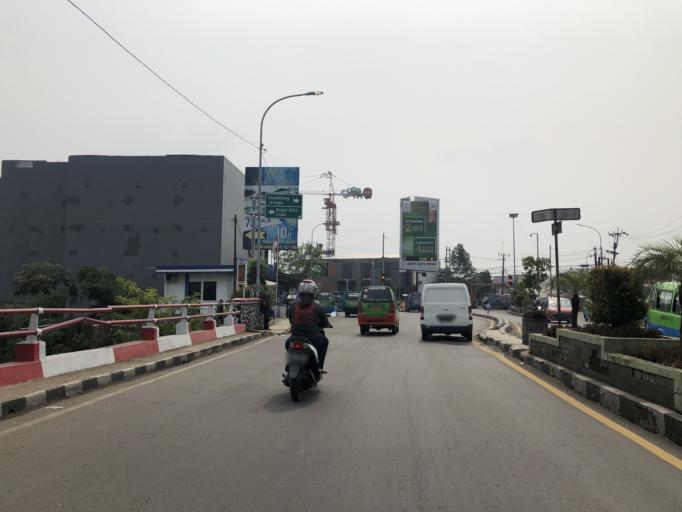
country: ID
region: West Java
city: Bogor
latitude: -6.5732
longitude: 106.7521
